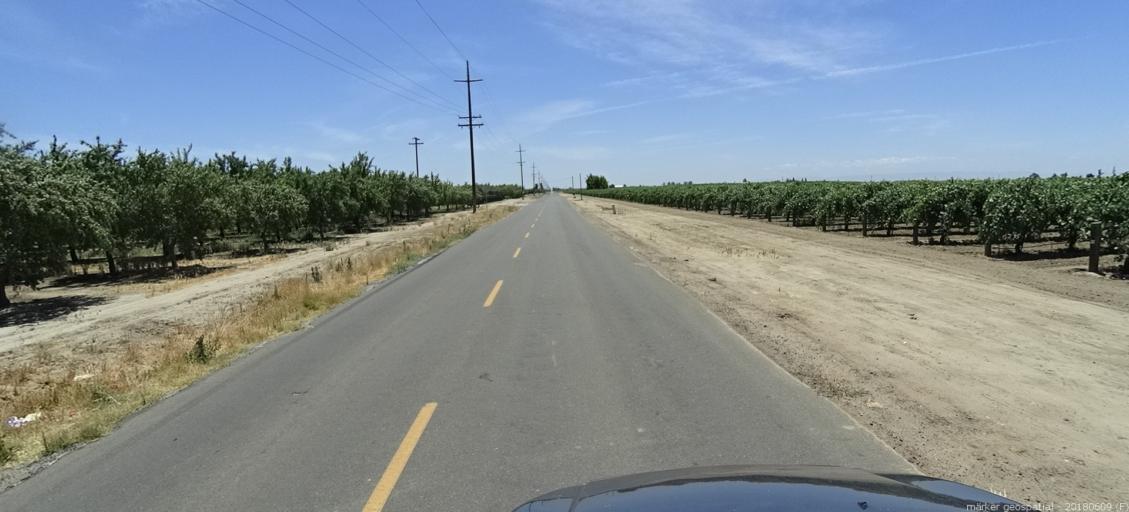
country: US
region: California
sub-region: Madera County
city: Parkwood
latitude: 36.9079
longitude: -120.1105
